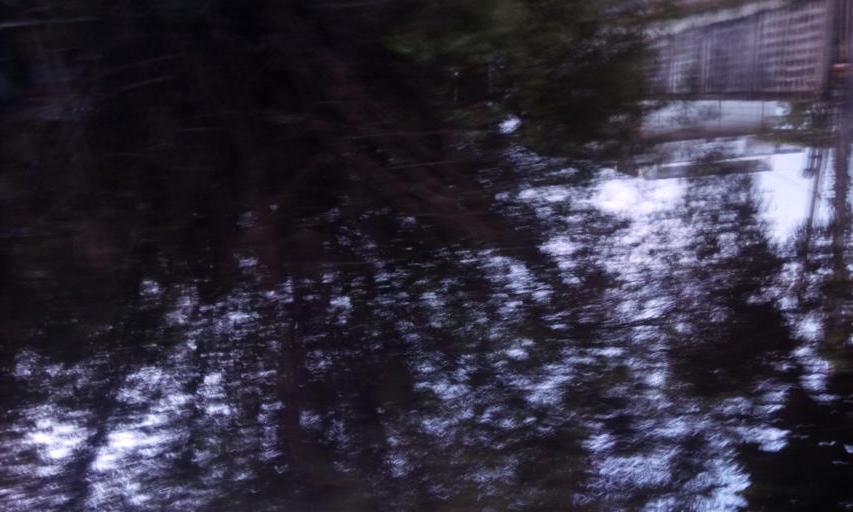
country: TH
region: Bangkok
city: Nong Chok
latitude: 13.8569
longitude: 100.8710
